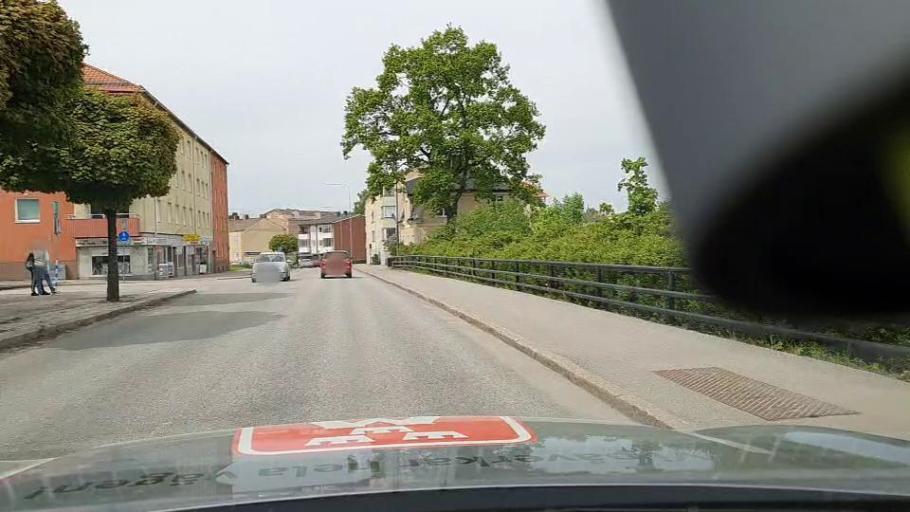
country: SE
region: Soedermanland
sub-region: Flens Kommun
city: Flen
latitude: 59.0567
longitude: 16.5954
